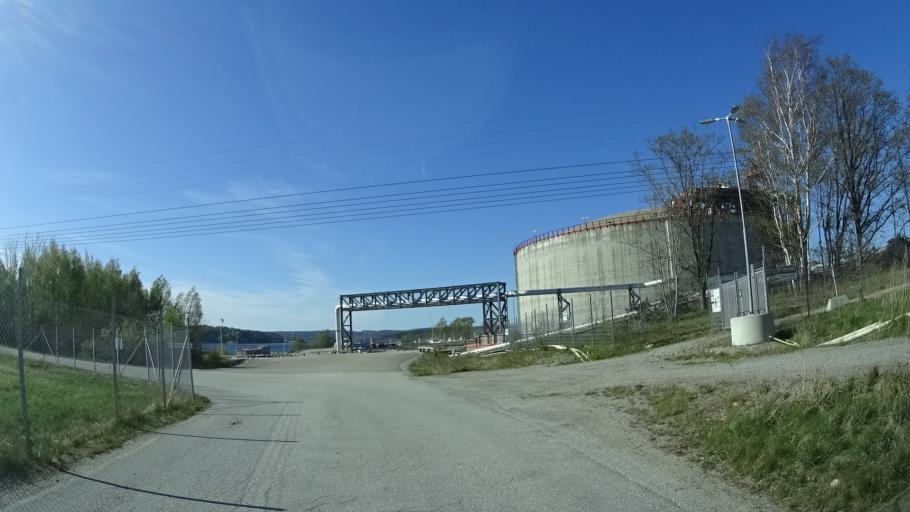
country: SE
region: Vaestra Goetaland
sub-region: Stenungsunds Kommun
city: Stenungsund
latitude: 58.0843
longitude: 11.8148
